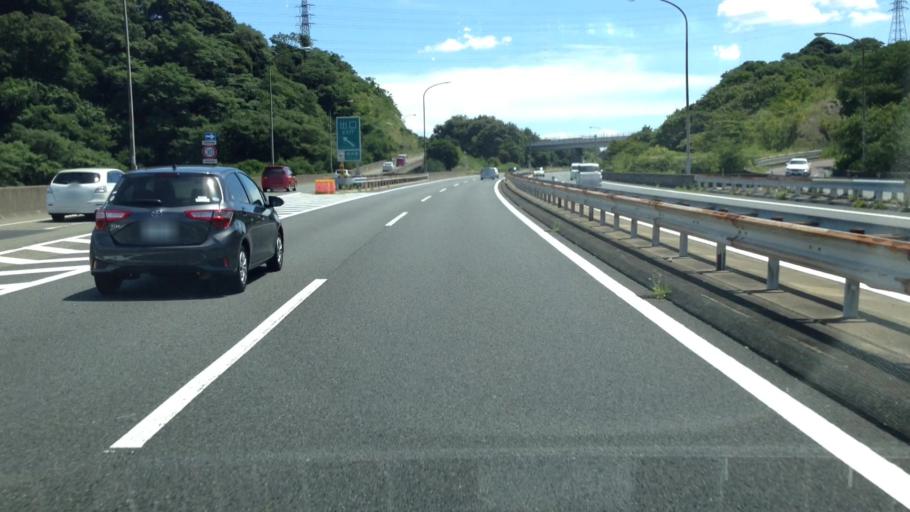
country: JP
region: Kanagawa
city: Yokosuka
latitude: 35.2793
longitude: 139.6321
